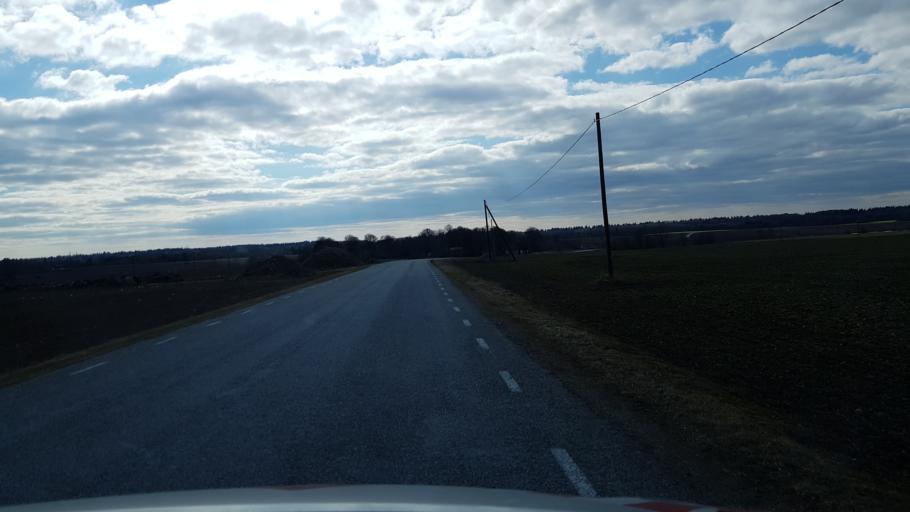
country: EE
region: Laeaene-Virumaa
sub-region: Kadrina vald
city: Kadrina
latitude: 59.2915
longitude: 26.1979
